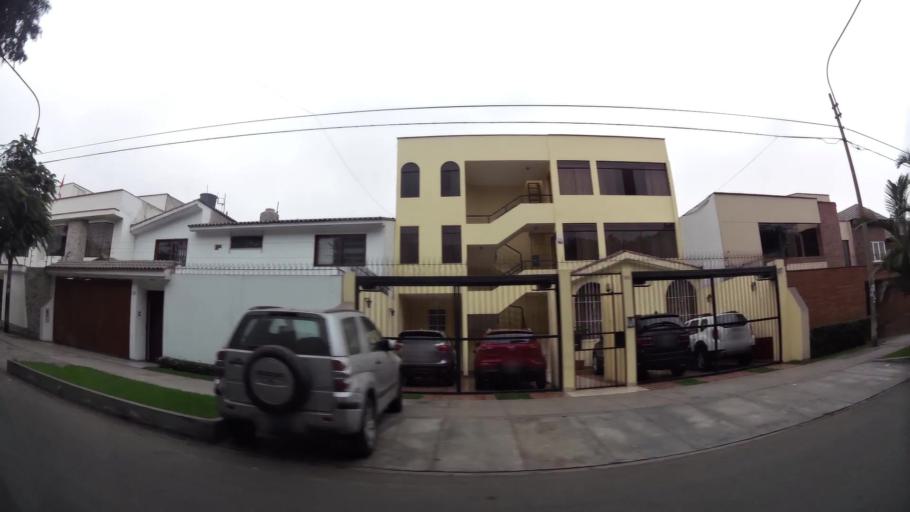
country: PE
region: Lima
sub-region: Lima
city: La Molina
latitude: -12.0933
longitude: -76.9481
